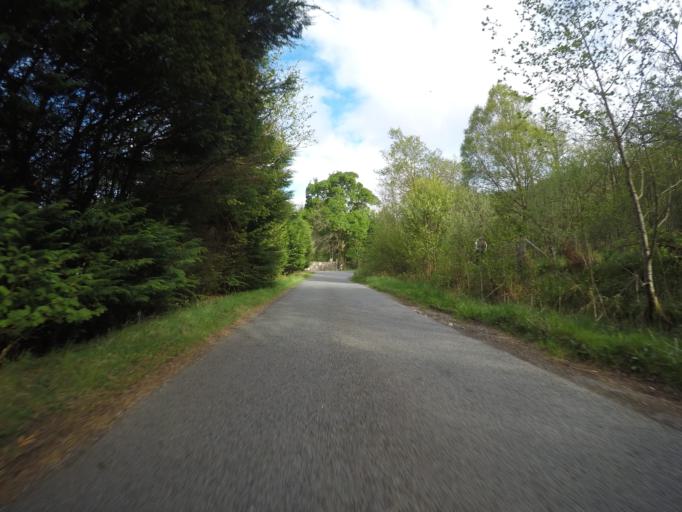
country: GB
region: Scotland
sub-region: Highland
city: Fort William
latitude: 56.6793
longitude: -5.0834
